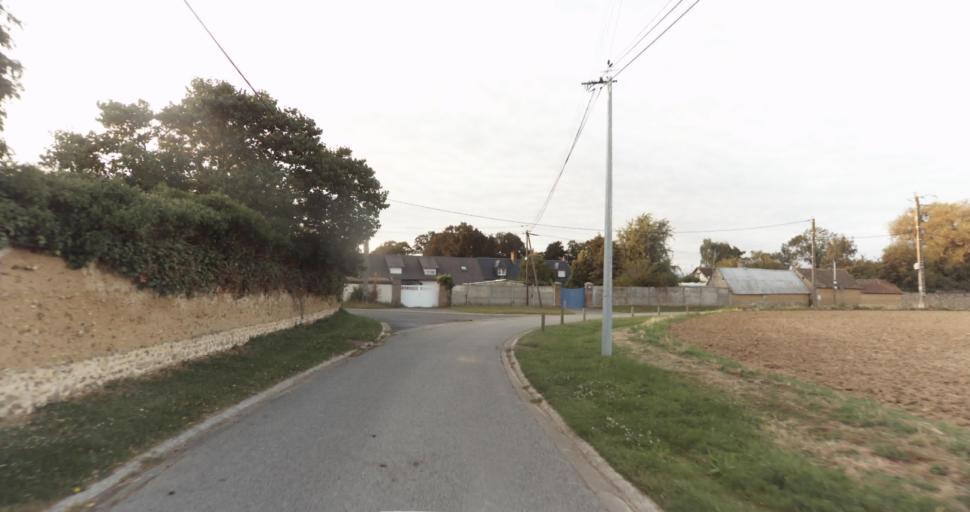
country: FR
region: Haute-Normandie
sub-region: Departement de l'Eure
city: La Madeleine-de-Nonancourt
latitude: 48.8742
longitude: 1.1855
